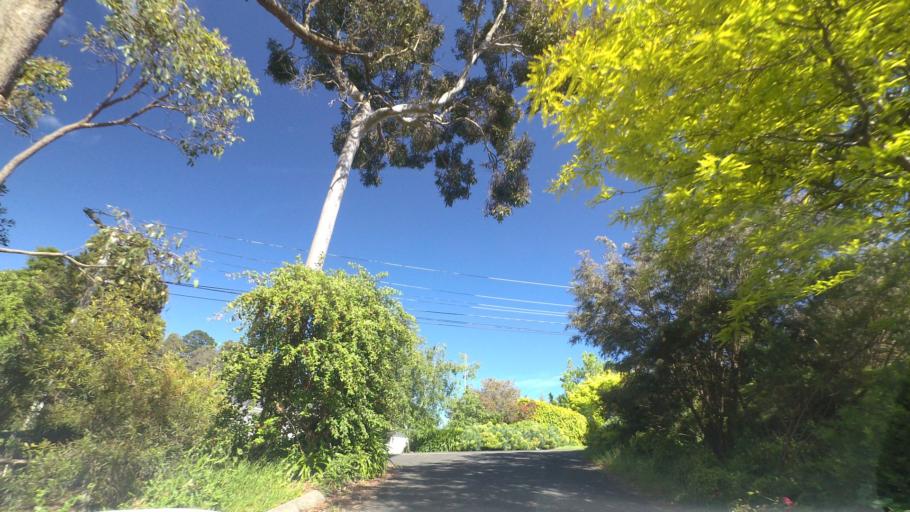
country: AU
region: Victoria
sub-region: Maroondah
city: Ringwood East
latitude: -37.8205
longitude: 145.2533
